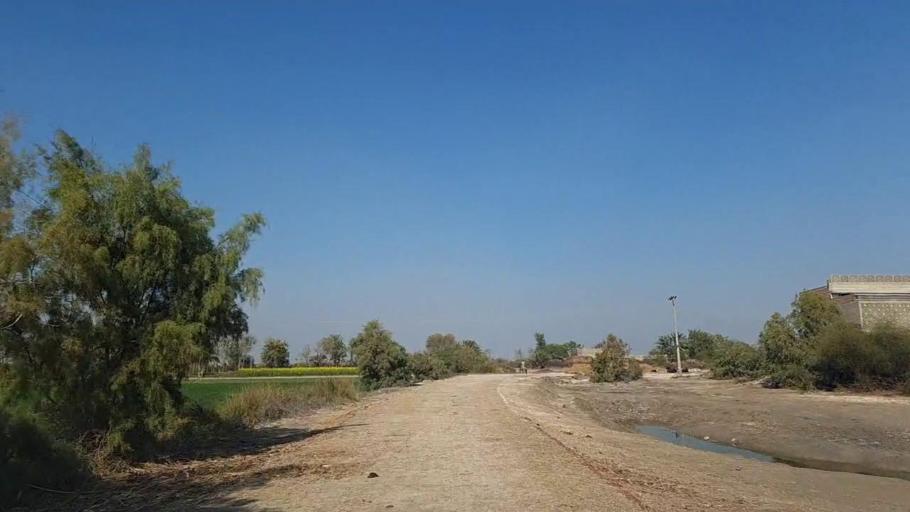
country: PK
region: Sindh
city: Bandhi
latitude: 26.5474
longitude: 68.3270
